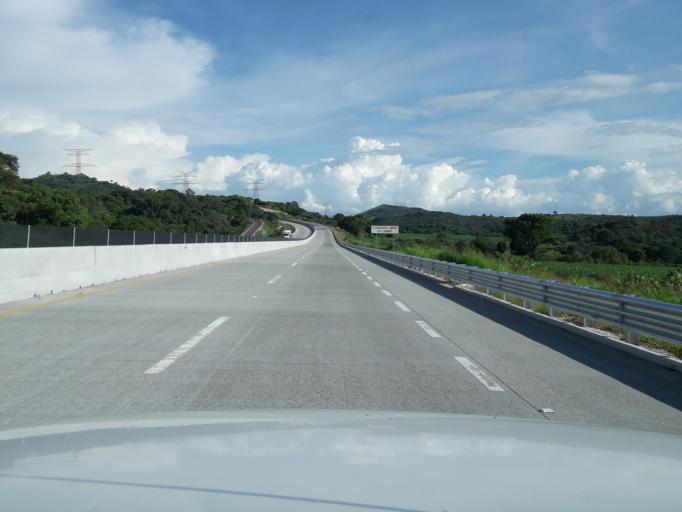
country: MX
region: Jalisco
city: Tala
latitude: 20.5906
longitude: -103.6707
